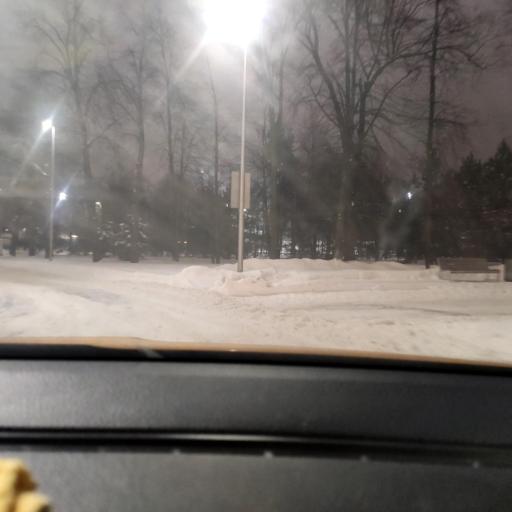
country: RU
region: Moscow
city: Luzhniki
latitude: 55.7172
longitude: 37.5522
